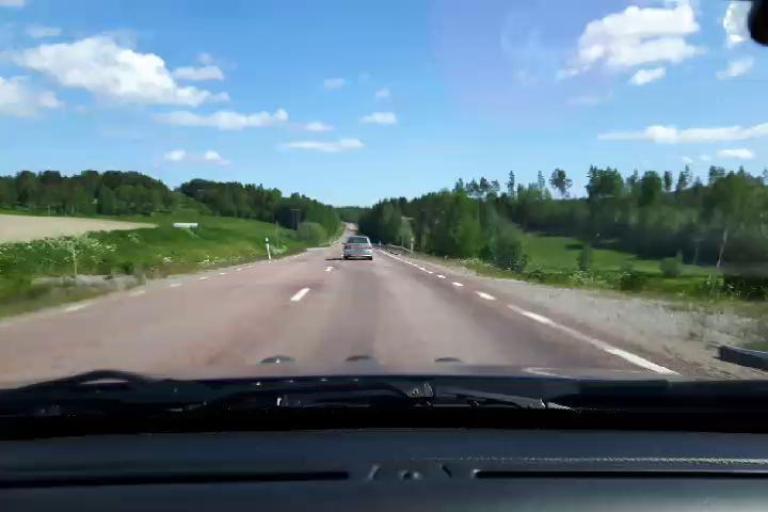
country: SE
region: Gaevleborg
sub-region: Hudiksvalls Kommun
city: Sorforsa
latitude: 61.7479
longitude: 16.8403
